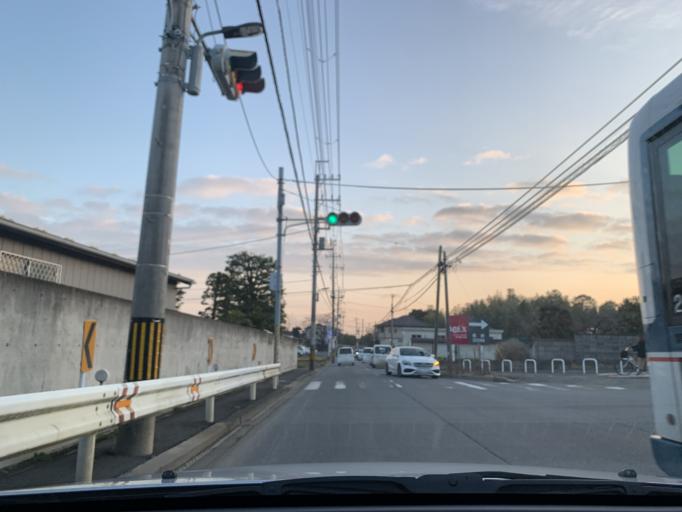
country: JP
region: Chiba
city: Matsudo
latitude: 35.7599
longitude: 139.9189
